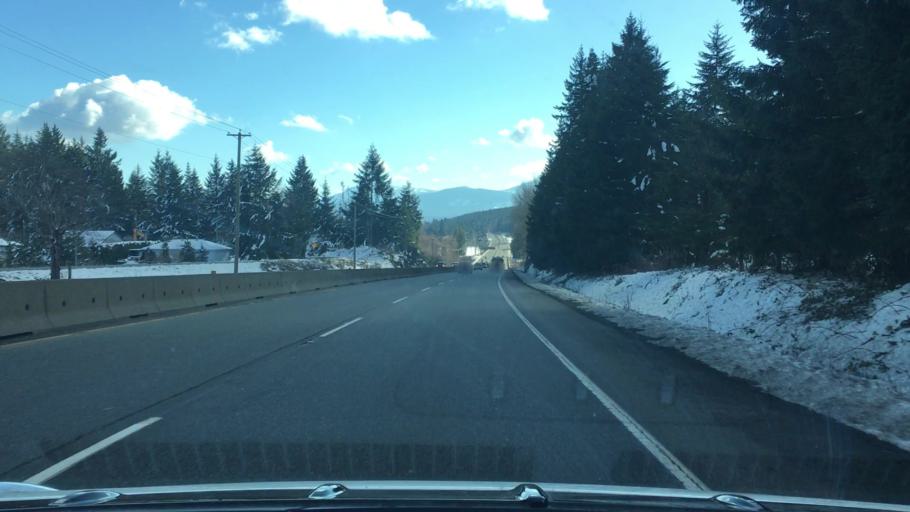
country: CA
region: British Columbia
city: Nanaimo
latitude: 49.0885
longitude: -123.8836
